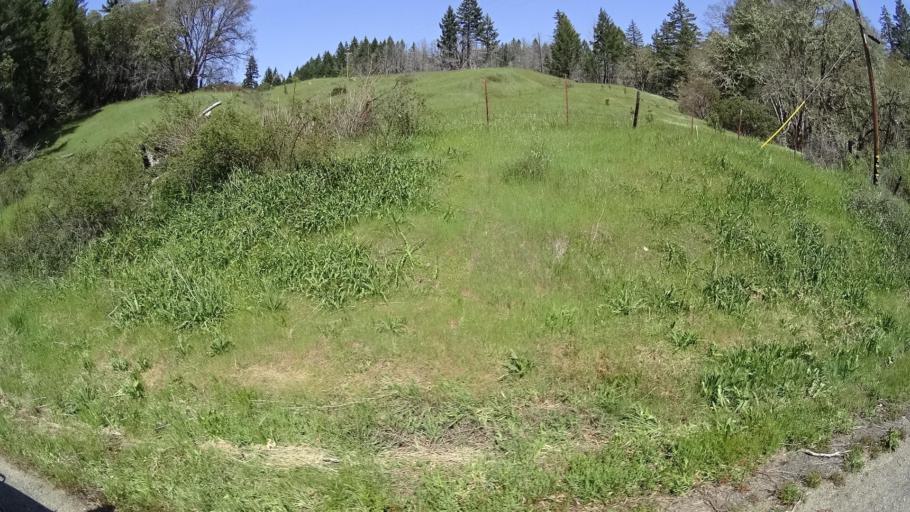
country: US
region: California
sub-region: Humboldt County
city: Redway
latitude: 40.2852
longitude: -123.6471
